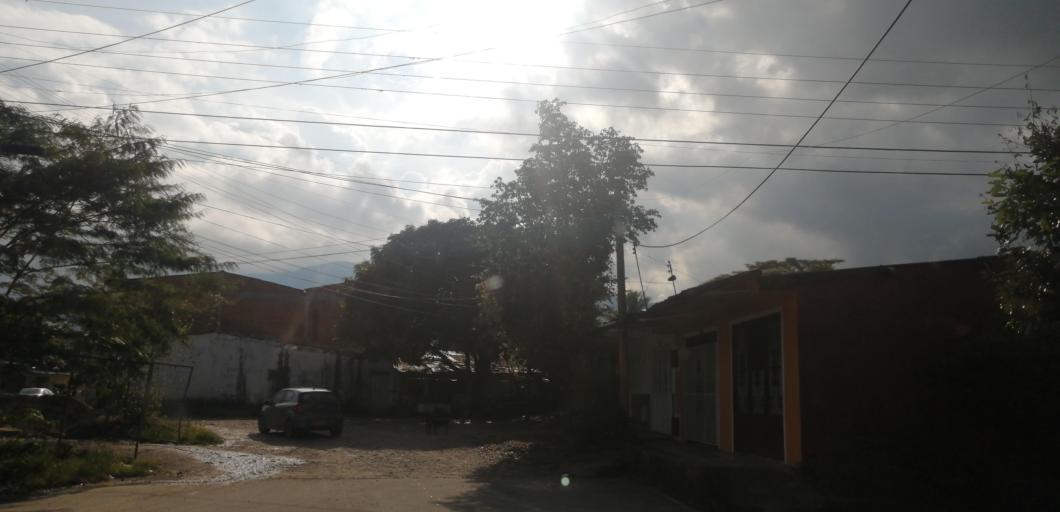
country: CO
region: Meta
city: Acacias
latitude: 3.9865
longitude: -73.7771
